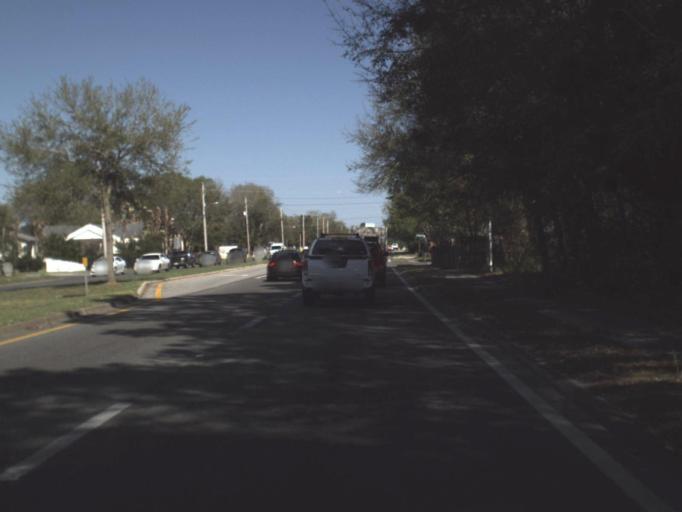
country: US
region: Florida
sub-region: Okaloosa County
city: Mary Esther
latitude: 30.4090
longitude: -86.6498
